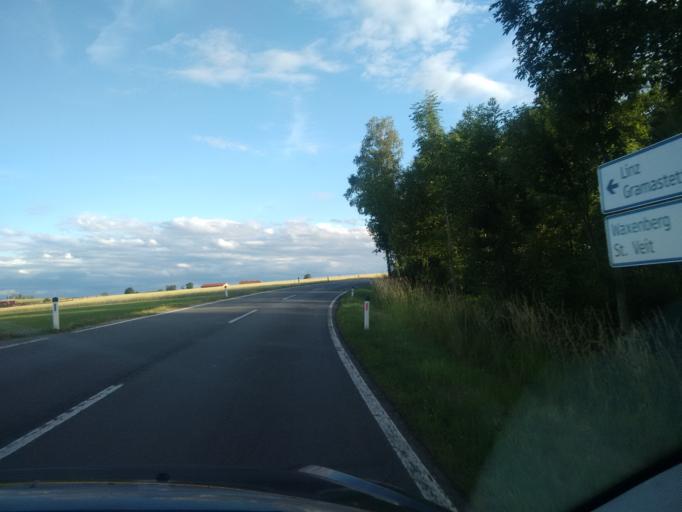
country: AT
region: Upper Austria
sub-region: Politischer Bezirk Urfahr-Umgebung
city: Gramastetten
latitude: 48.4037
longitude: 14.1823
